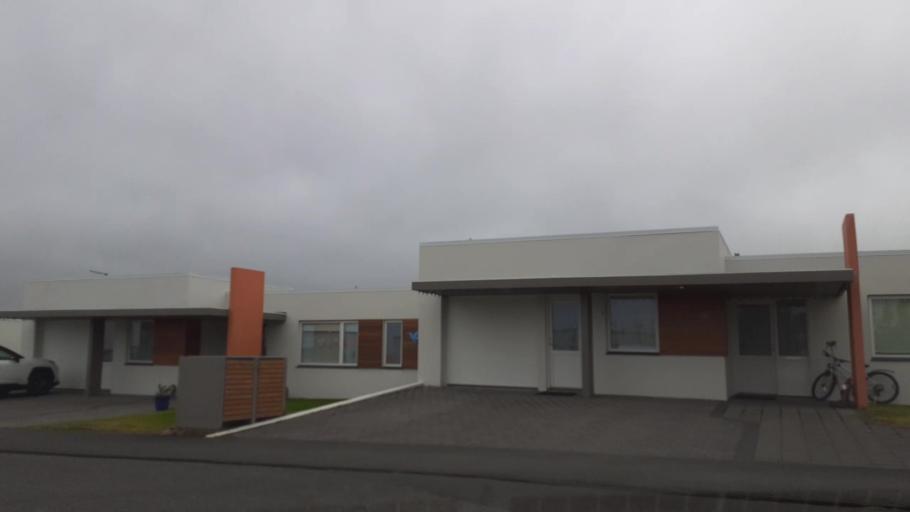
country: IS
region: Northeast
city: Dalvik
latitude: 65.9731
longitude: -18.5349
